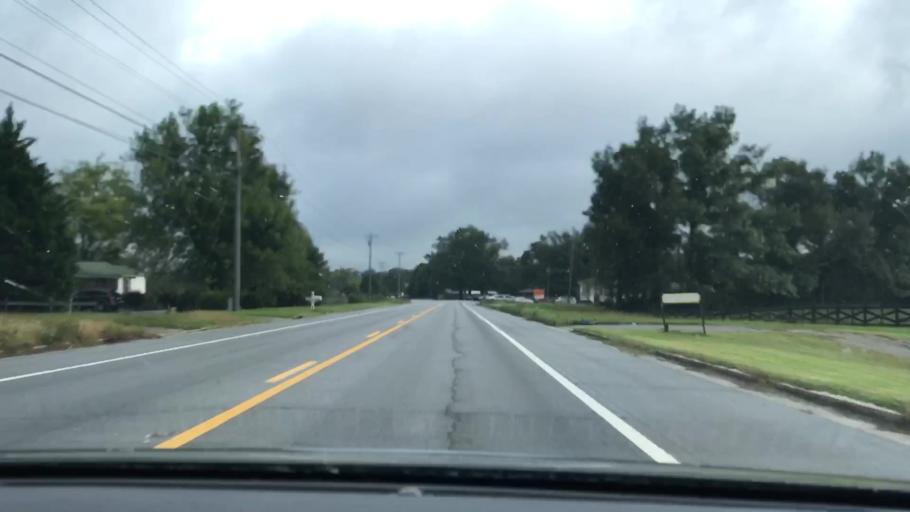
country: US
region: Tennessee
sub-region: Fentress County
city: Grimsley
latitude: 36.2533
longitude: -84.9918
